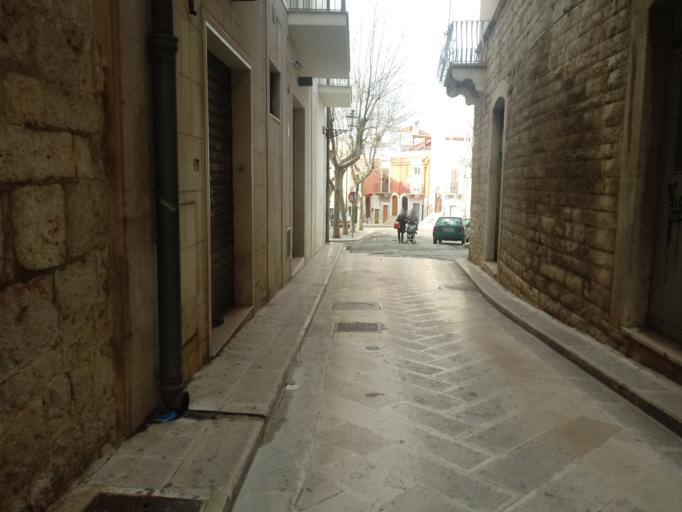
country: IT
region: Apulia
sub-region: Provincia di Barletta - Andria - Trani
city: Andria
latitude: 41.2266
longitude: 16.2943
